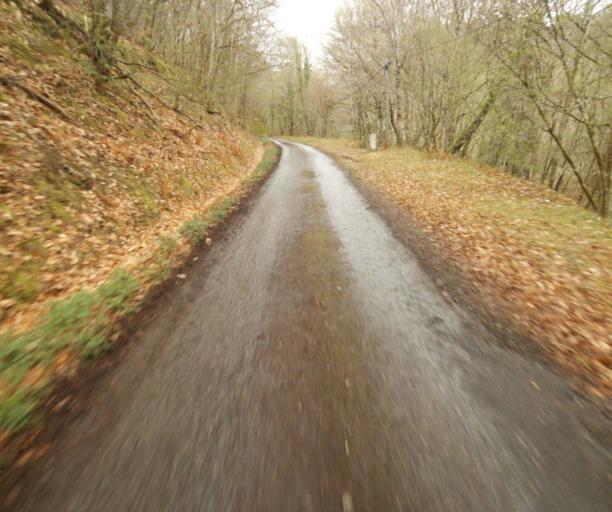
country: FR
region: Limousin
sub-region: Departement de la Correze
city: Saint-Privat
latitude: 45.2180
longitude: 2.0348
